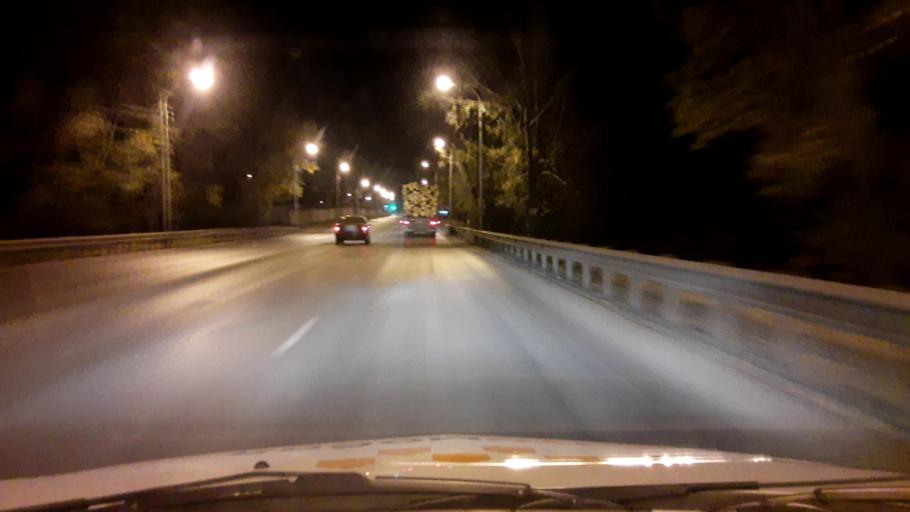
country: RU
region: Bashkortostan
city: Iglino
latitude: 54.7855
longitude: 56.2205
